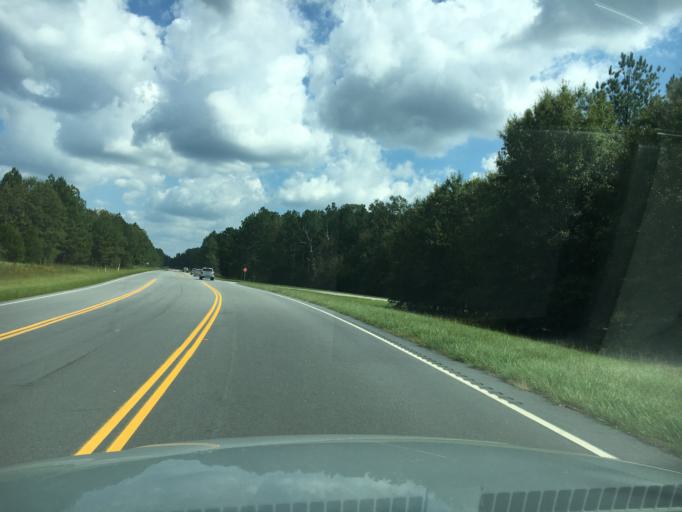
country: US
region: South Carolina
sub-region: Greenwood County
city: Greenwood
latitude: 34.1374
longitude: -82.1401
